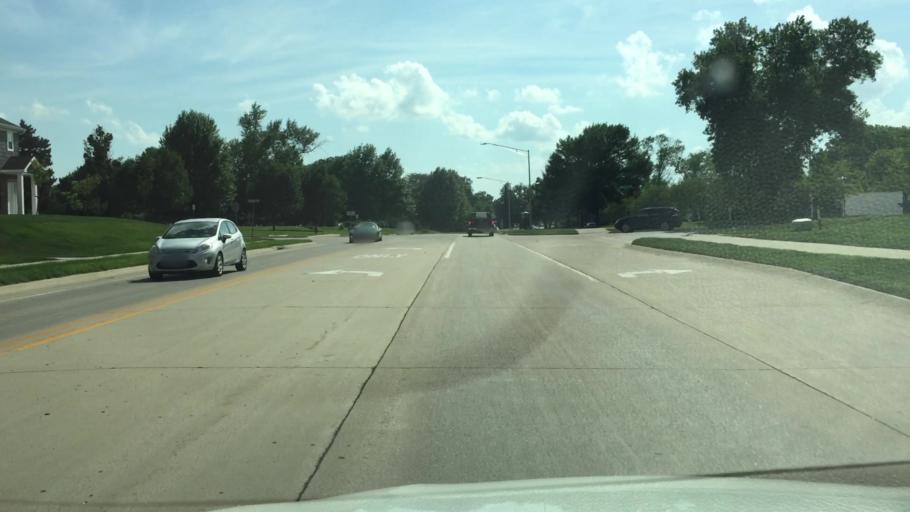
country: US
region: Iowa
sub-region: Johnson County
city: Iowa City
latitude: 41.6774
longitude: -91.5160
